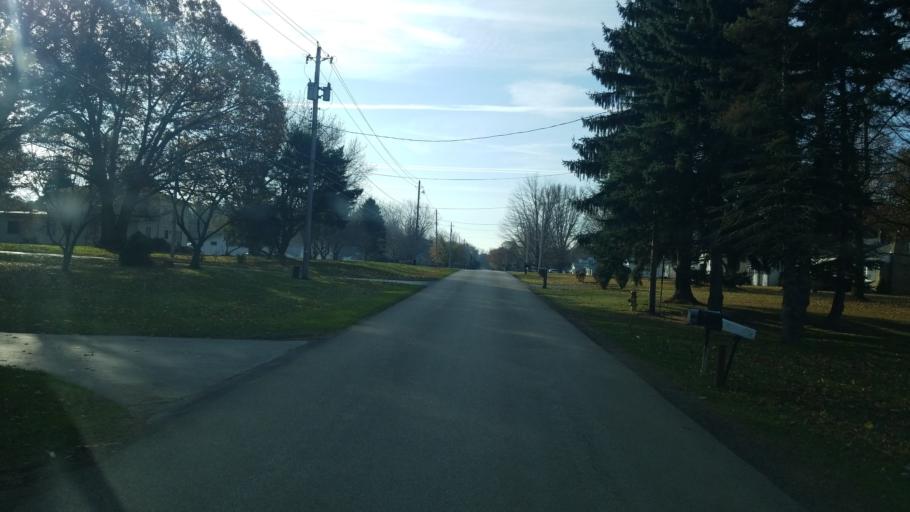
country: US
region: Ohio
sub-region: Ashtabula County
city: North Kingsville
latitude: 41.9295
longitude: -80.6473
